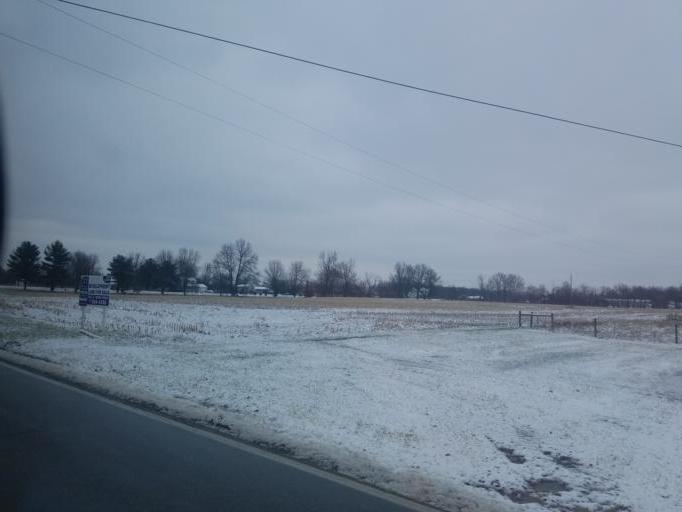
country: US
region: Ohio
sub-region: Franklin County
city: New Albany
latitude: 40.0959
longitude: -82.7639
